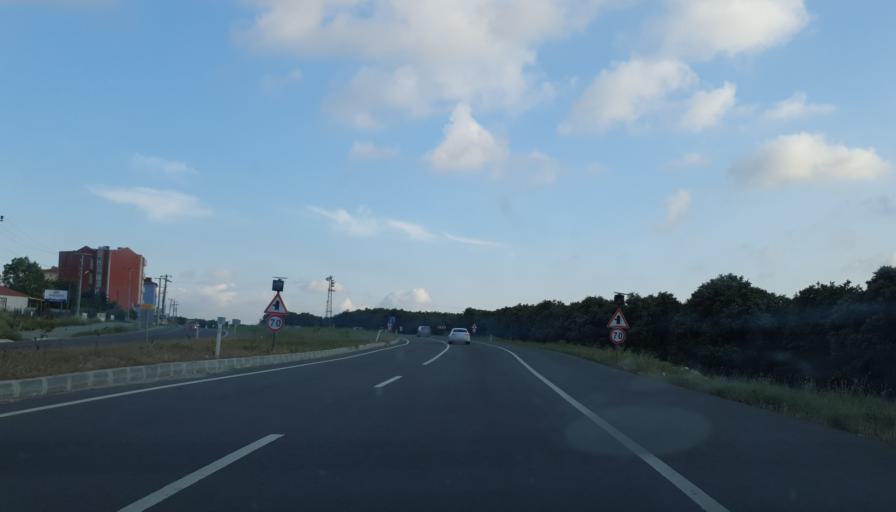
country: TR
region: Tekirdag
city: Saray
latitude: 41.3657
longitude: 27.9415
